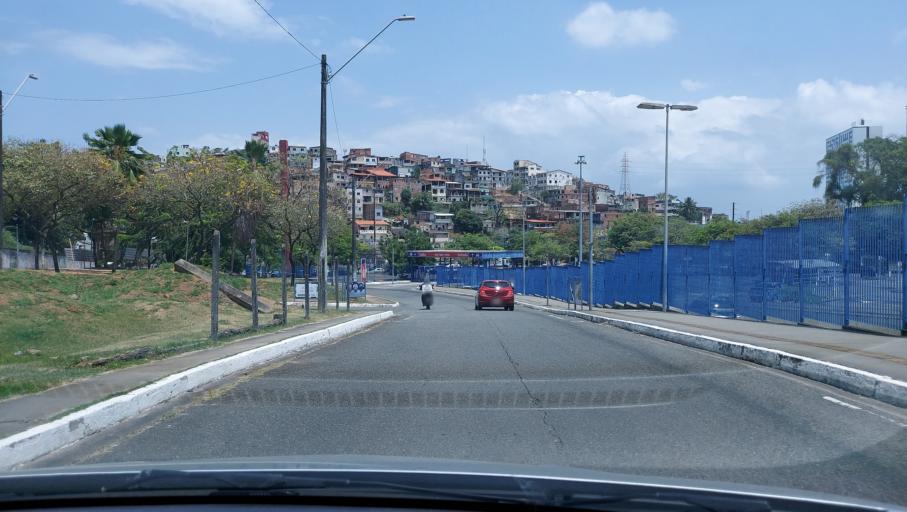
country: BR
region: Bahia
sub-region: Salvador
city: Salvador
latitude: -12.9995
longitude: -38.4903
